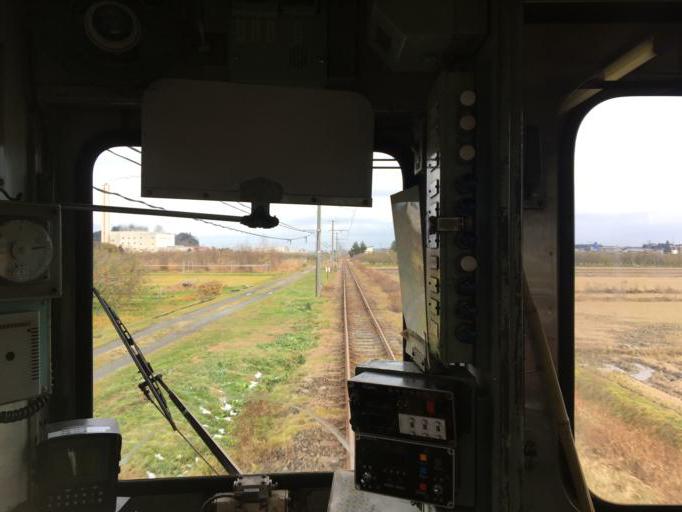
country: JP
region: Aomori
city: Hirosaki
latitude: 40.5391
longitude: 140.5518
